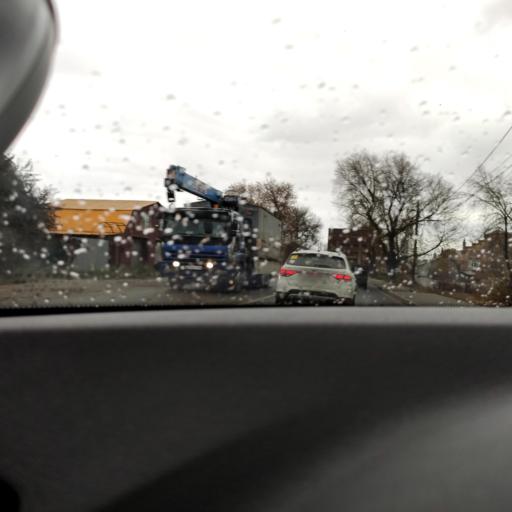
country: RU
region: Samara
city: Smyshlyayevka
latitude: 53.2376
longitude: 50.3205
